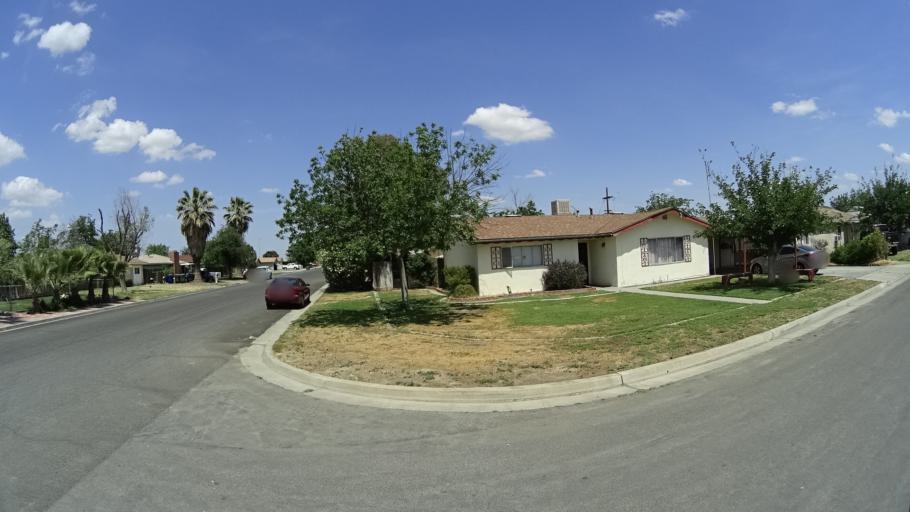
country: US
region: California
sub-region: Kings County
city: Stratford
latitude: 36.1939
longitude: -119.8225
